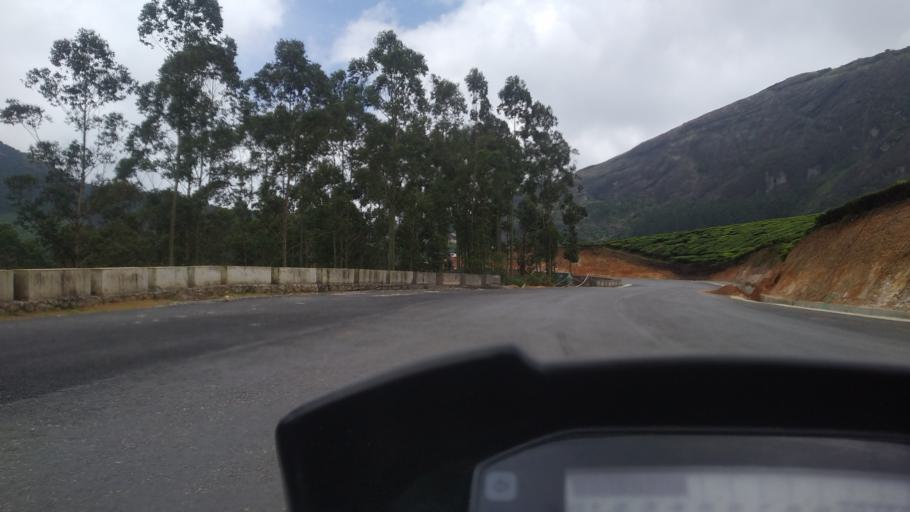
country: IN
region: Kerala
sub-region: Idukki
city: Munnar
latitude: 10.0470
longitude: 77.1138
